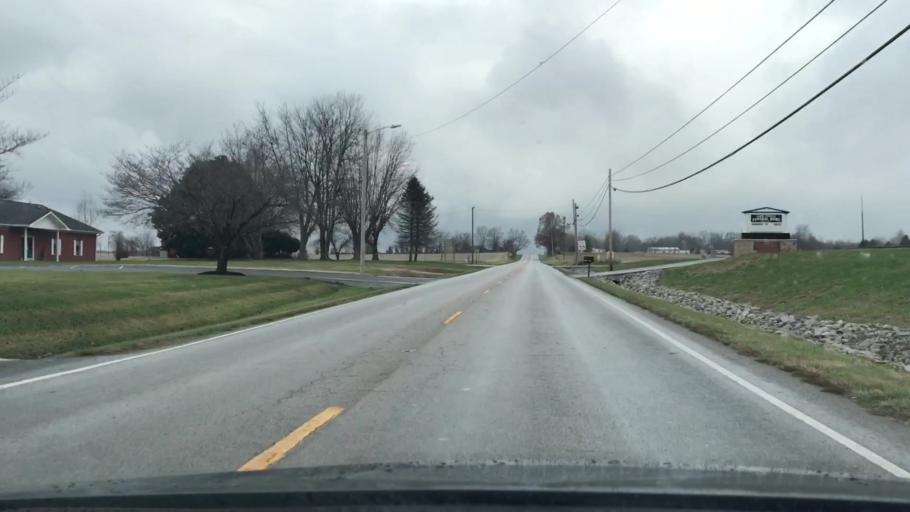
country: US
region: Kentucky
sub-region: Todd County
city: Elkton
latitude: 36.8145
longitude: -87.1757
